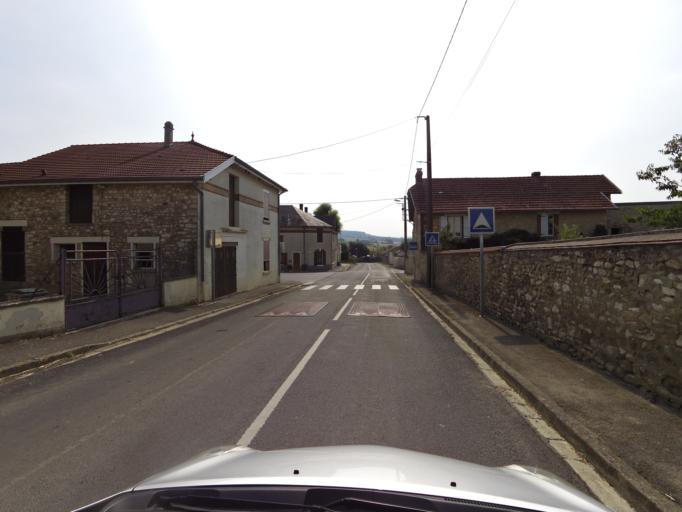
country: FR
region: Champagne-Ardenne
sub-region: Departement de la Marne
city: Gueux
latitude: 49.1668
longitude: 3.8916
